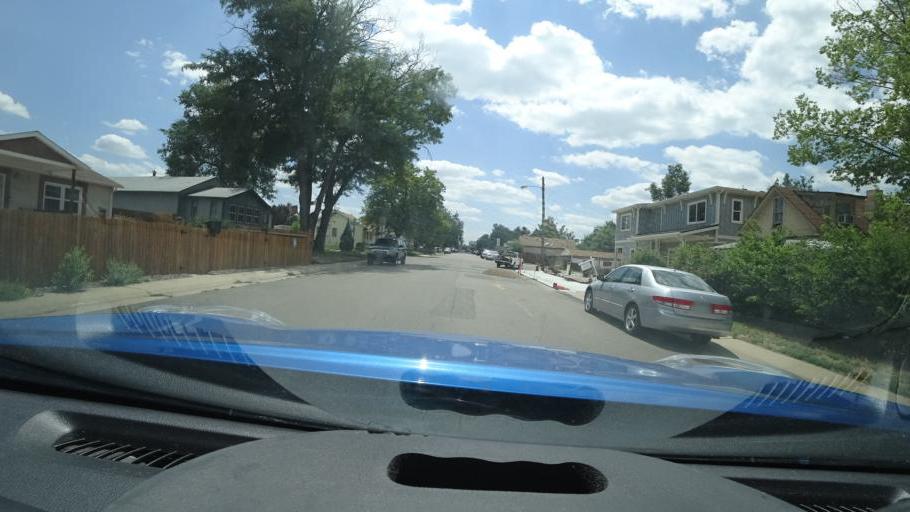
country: US
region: Colorado
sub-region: Arapahoe County
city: Englewood
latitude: 39.6734
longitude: -104.9960
